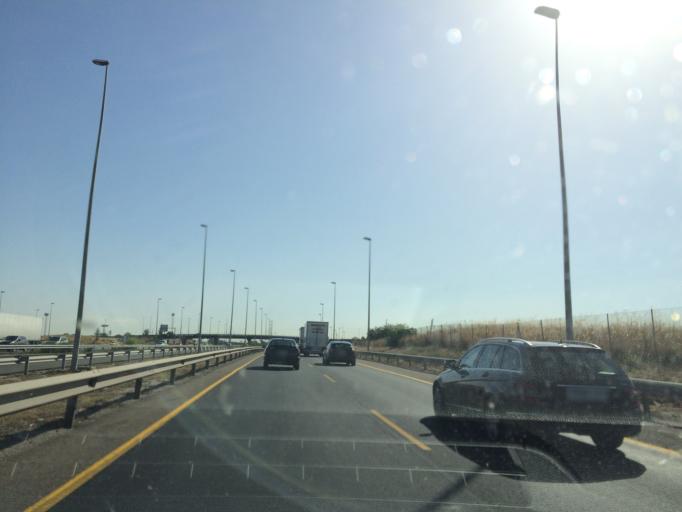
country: ES
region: Madrid
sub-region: Provincia de Madrid
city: Mostoles
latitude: 40.3405
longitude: -3.8709
